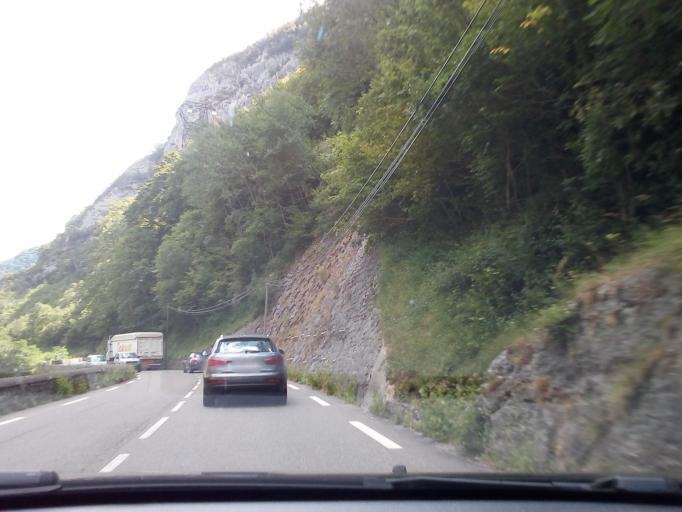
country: FR
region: Aquitaine
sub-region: Departement des Pyrenees-Atlantiques
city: Laruns
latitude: 42.8868
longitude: -0.5633
